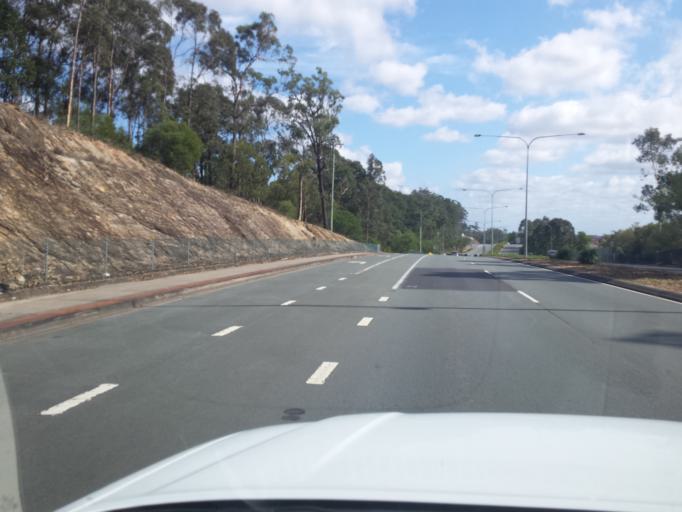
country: AU
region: Queensland
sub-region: Brisbane
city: Bridegman Downs
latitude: -27.3769
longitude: 152.9804
